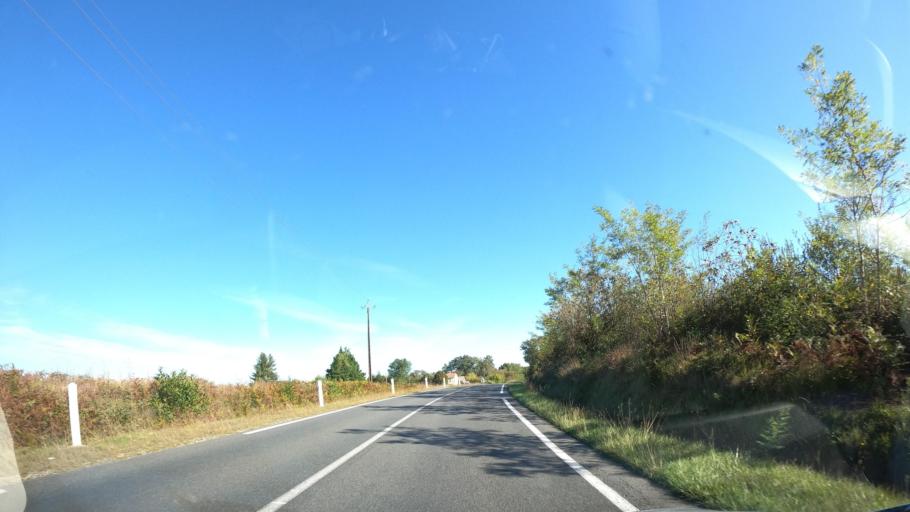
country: FR
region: Aquitaine
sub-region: Departement de la Dordogne
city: Vergt
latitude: 45.0111
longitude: 0.6055
